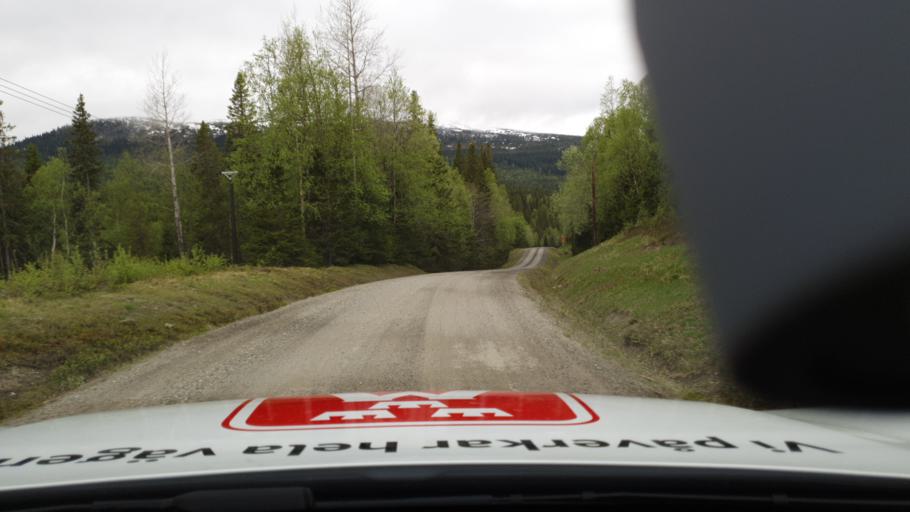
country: NO
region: Nord-Trondelag
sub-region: Lierne
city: Sandvika
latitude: 64.4532
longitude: 14.1610
